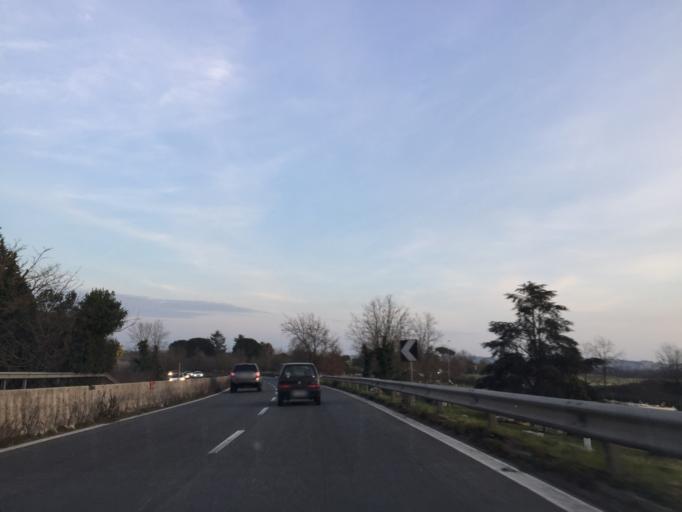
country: IT
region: Latium
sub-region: Citta metropolitana di Roma Capitale
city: Le Rughe
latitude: 42.0550
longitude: 12.3731
